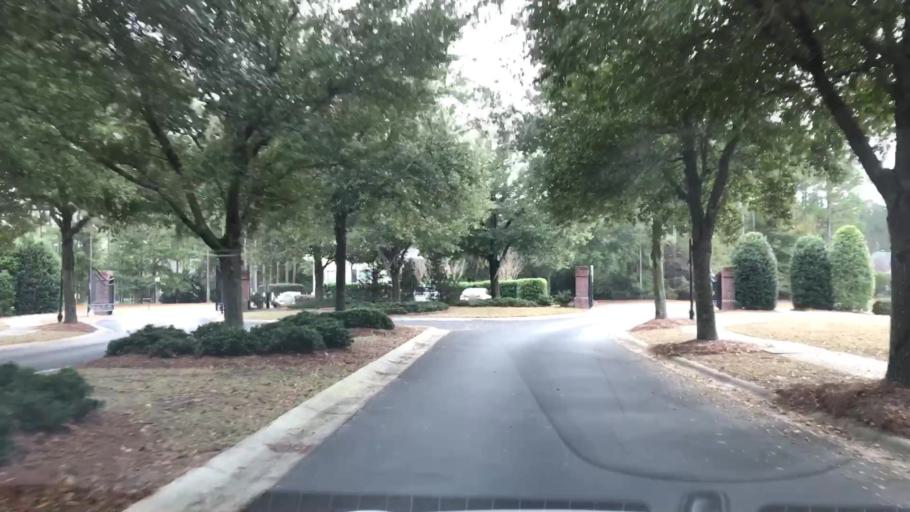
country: US
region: South Carolina
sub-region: Beaufort County
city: Bluffton
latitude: 32.2764
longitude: -80.9300
